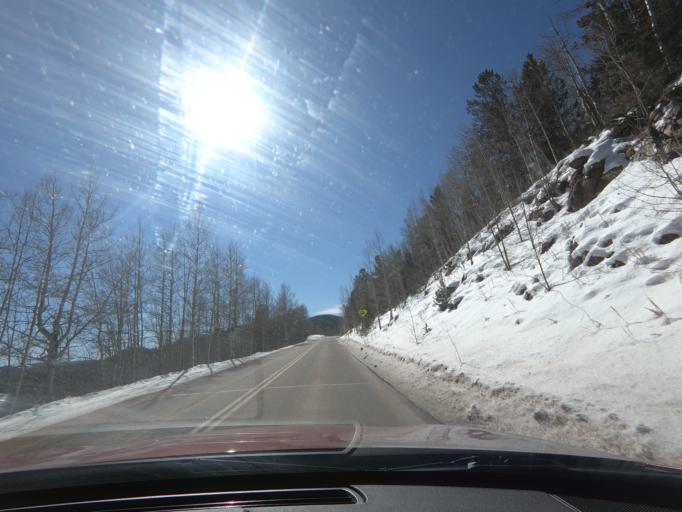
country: US
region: Colorado
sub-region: Teller County
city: Cripple Creek
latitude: 38.7463
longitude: -105.1002
